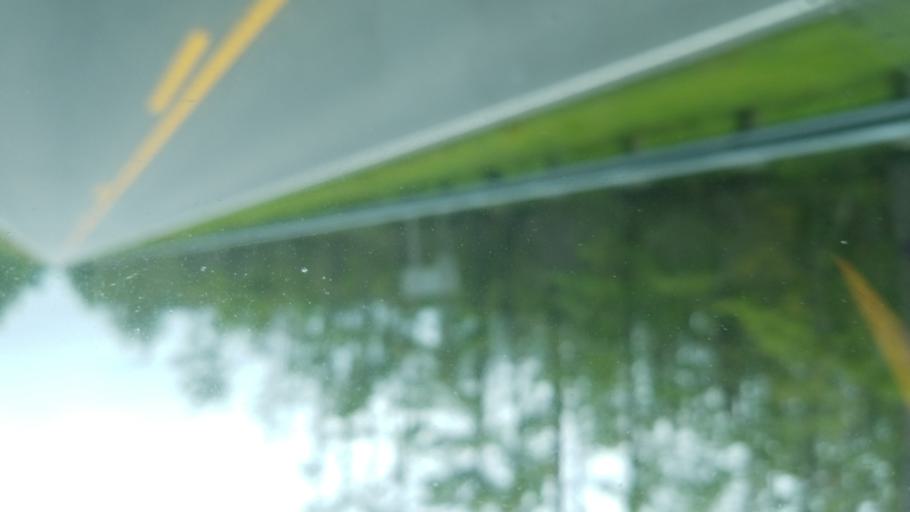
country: US
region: North Carolina
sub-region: Tyrrell County
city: Columbia
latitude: 35.8995
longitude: -76.0770
